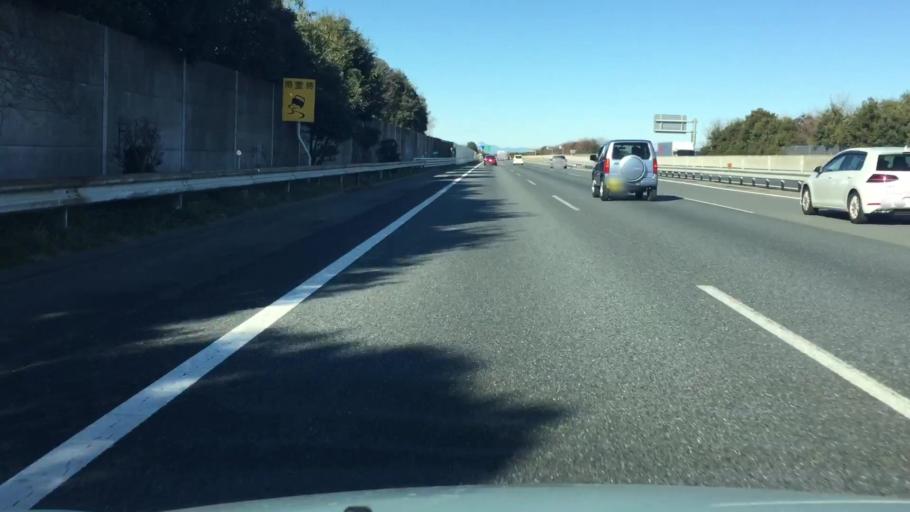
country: JP
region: Saitama
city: Yorii
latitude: 36.1277
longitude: 139.2423
